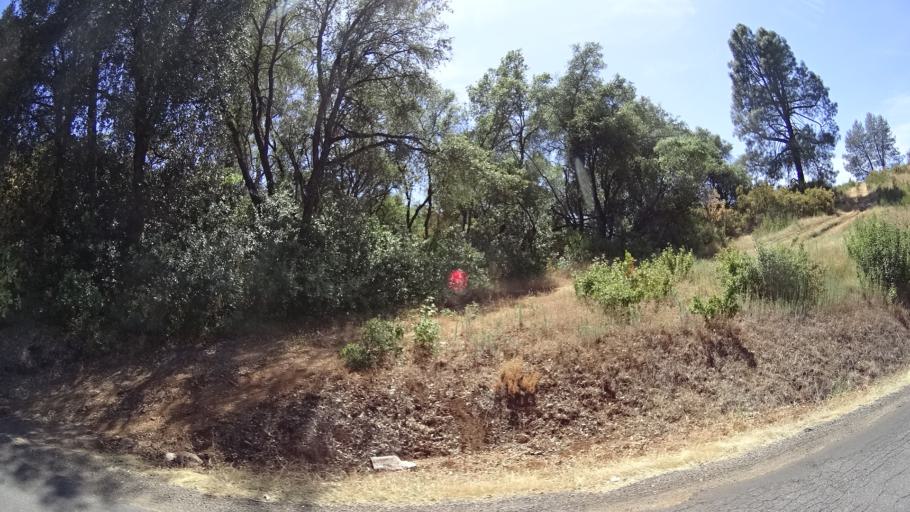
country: US
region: California
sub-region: Calaveras County
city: Murphys
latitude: 38.1487
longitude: -120.4739
